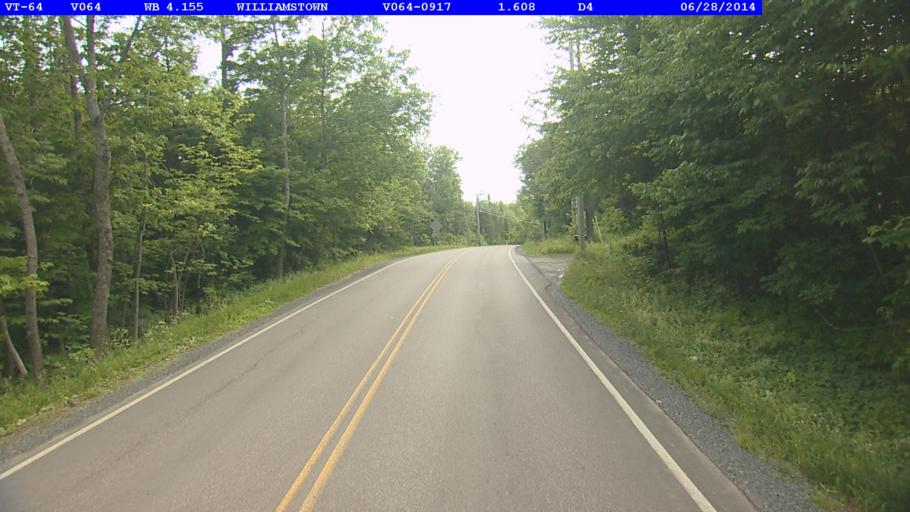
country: US
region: Vermont
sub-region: Orange County
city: Williamstown
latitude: 44.1105
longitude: -72.5839
